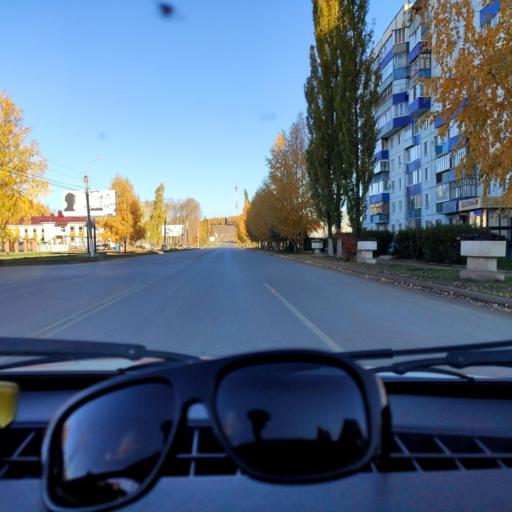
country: RU
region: Bashkortostan
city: Blagoveshchensk
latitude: 55.0514
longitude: 55.9530
